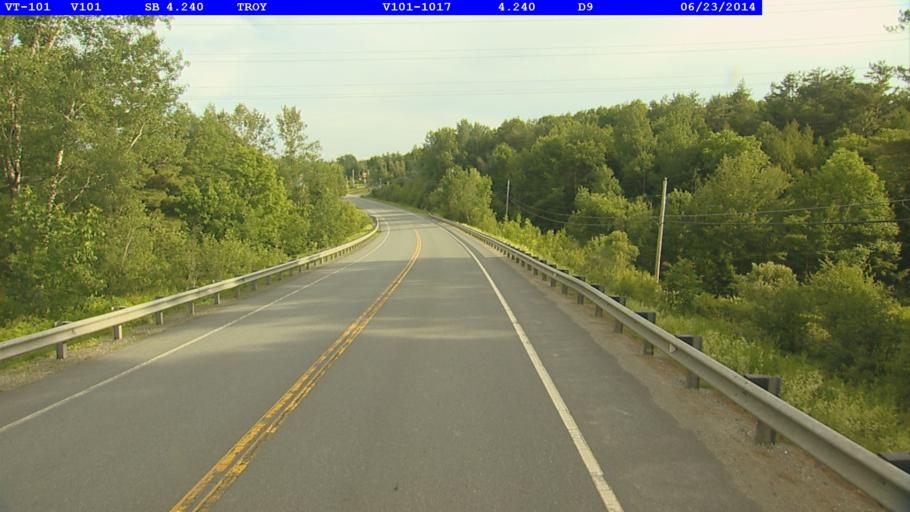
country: US
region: Vermont
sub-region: Orleans County
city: Newport
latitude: 44.9634
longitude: -72.4137
